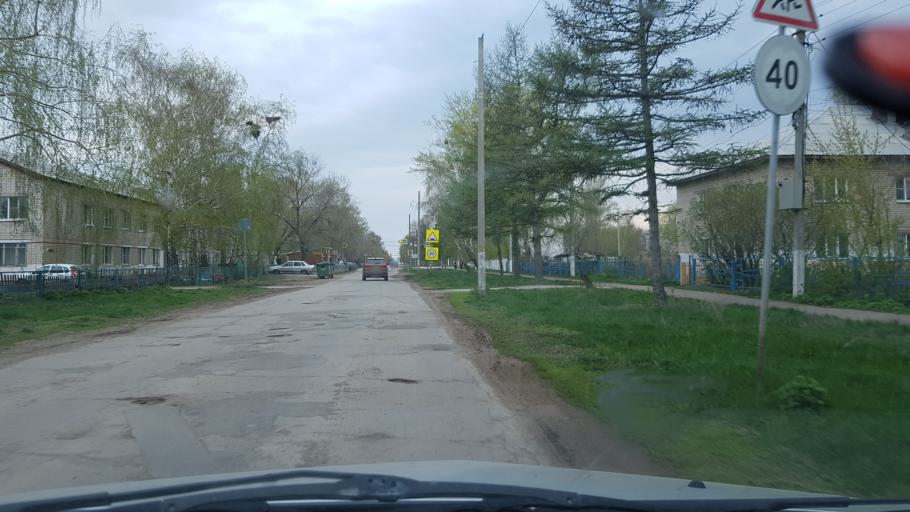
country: RU
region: Samara
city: Khryashchevka
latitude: 53.6721
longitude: 49.0724
